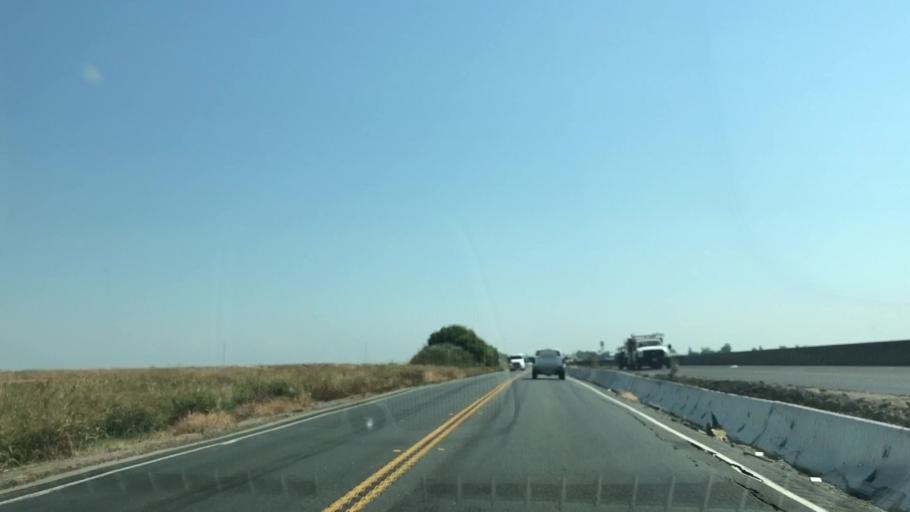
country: US
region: California
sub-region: Sacramento County
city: Walnut Grove
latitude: 38.1138
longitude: -121.5107
